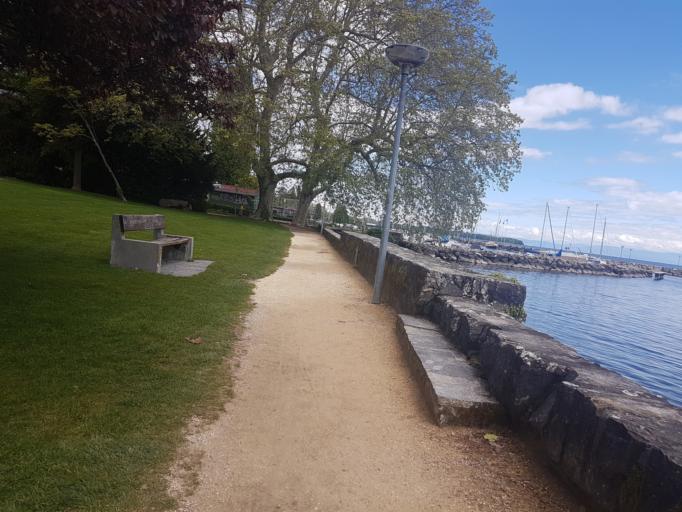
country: CH
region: Vaud
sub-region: Nyon District
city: Nyon
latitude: 46.3775
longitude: 6.2378
